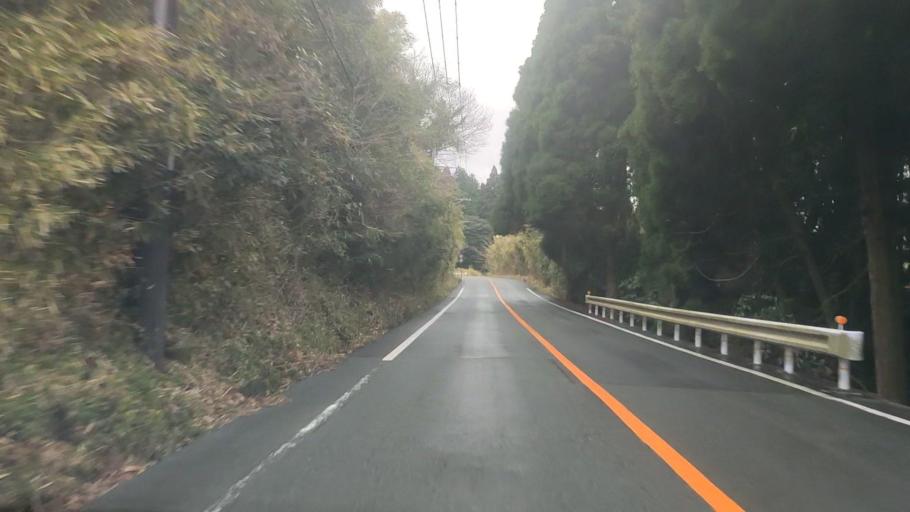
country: JP
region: Kumamoto
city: Aso
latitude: 32.8931
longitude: 131.0194
